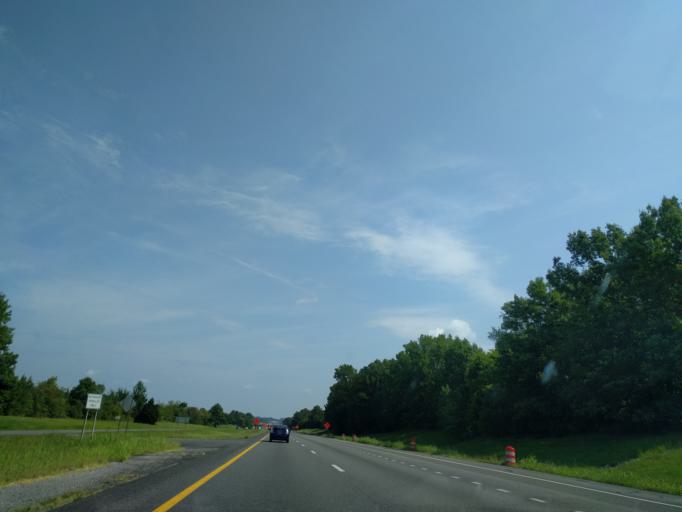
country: US
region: Tennessee
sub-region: Sumner County
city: Portland
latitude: 36.6135
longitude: -86.5791
